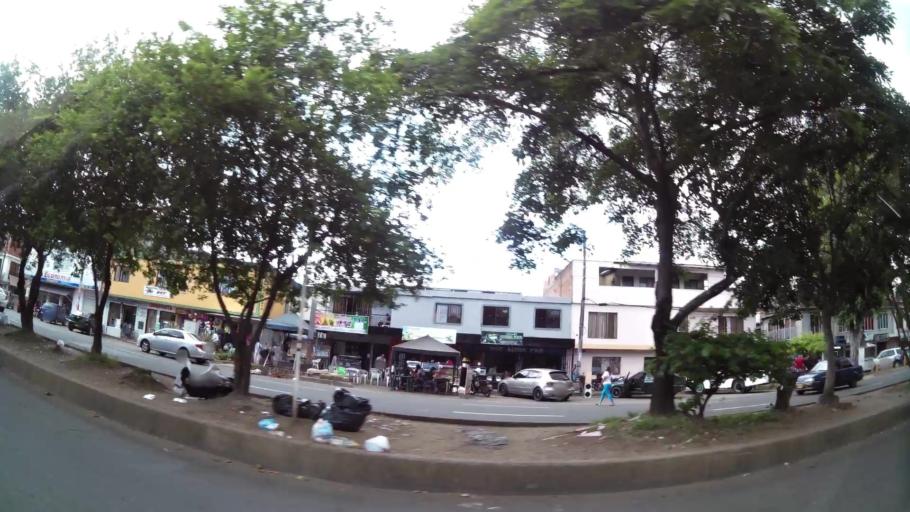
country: CO
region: Valle del Cauca
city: Cali
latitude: 3.4024
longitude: -76.5036
